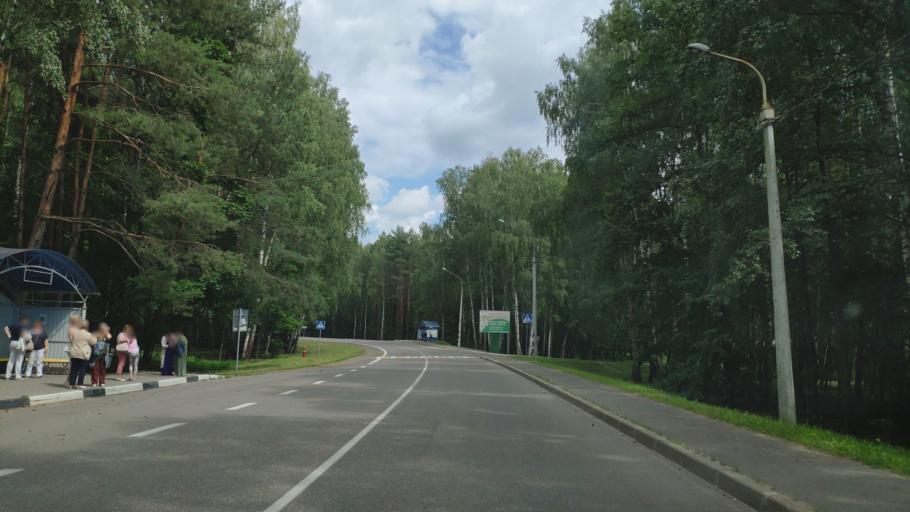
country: BY
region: Minsk
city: Zhdanovichy
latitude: 53.9684
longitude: 27.4284
